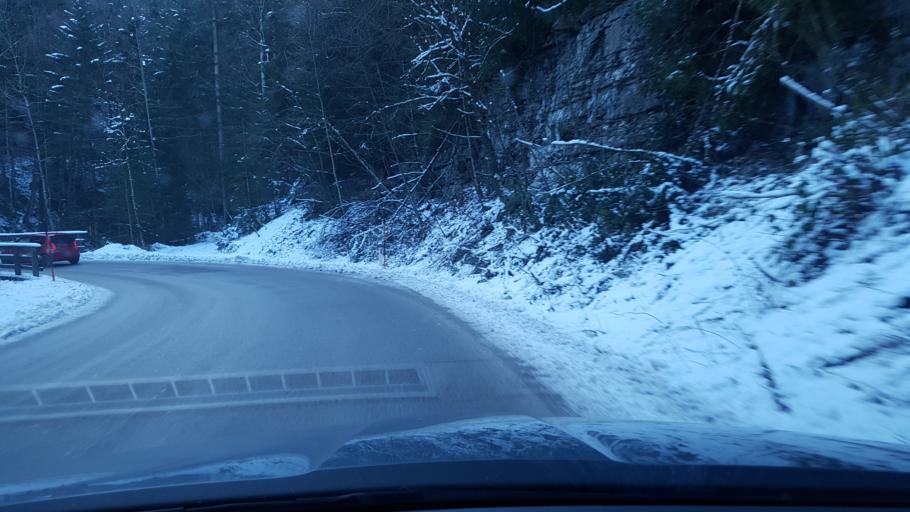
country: AT
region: Salzburg
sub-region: Politischer Bezirk Hallein
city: Scheffau am Tennengebirge
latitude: 47.6487
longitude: 13.2083
